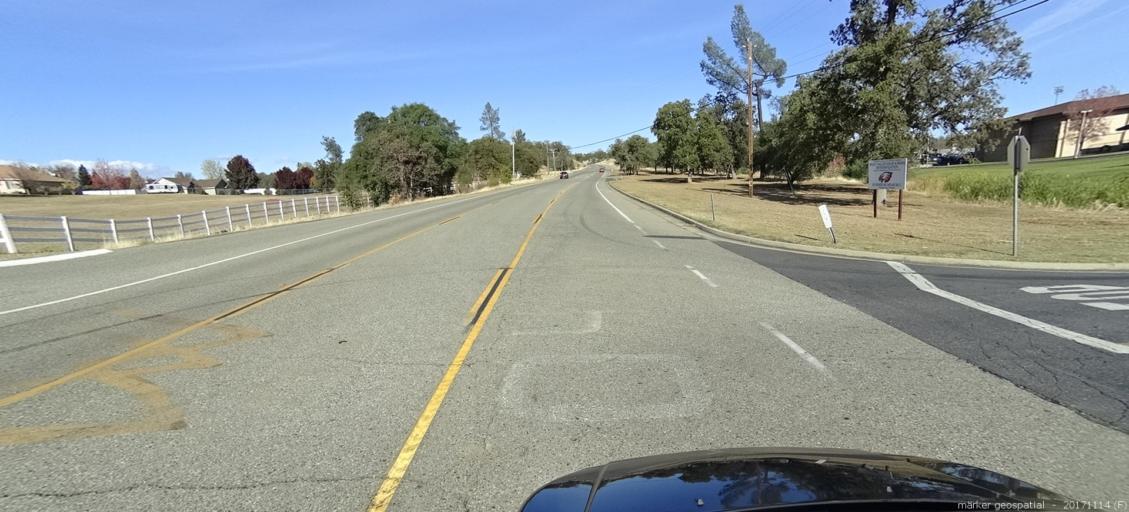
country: US
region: California
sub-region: Shasta County
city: Anderson
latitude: 40.3964
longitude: -122.4067
